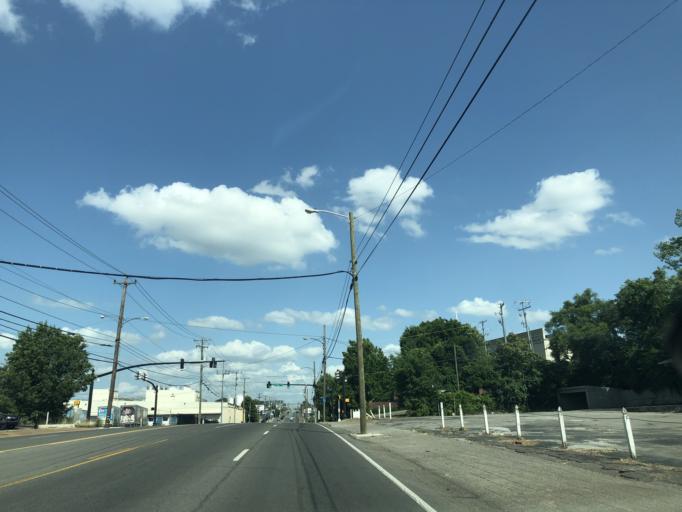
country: US
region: Tennessee
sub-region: Davidson County
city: Nashville
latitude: 36.1463
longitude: -86.7549
